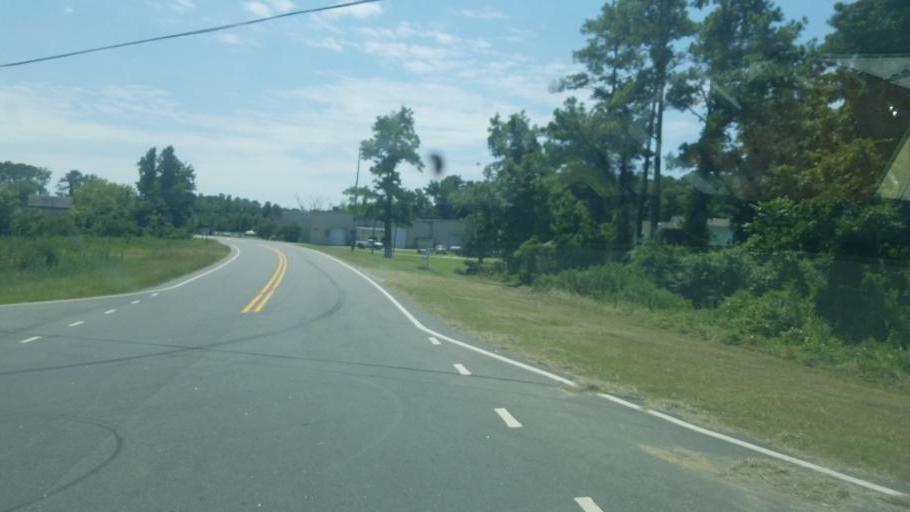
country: US
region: North Carolina
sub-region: Dare County
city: Manteo
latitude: 35.9064
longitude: -75.7745
